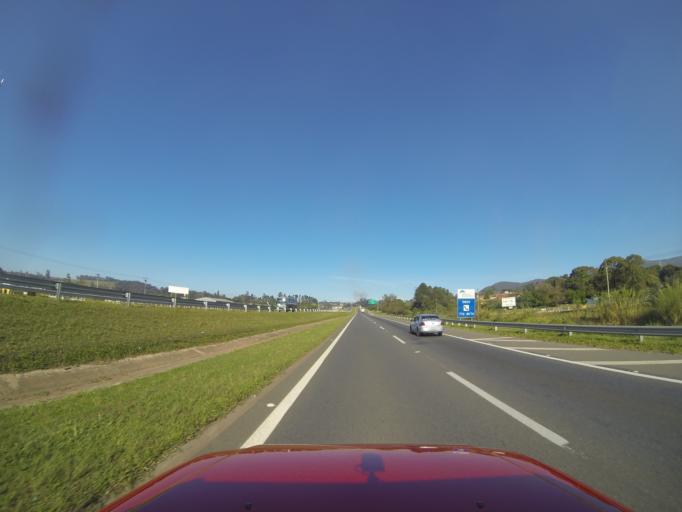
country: BR
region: Sao Paulo
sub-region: Atibaia
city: Atibaia
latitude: -23.1081
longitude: -46.5273
